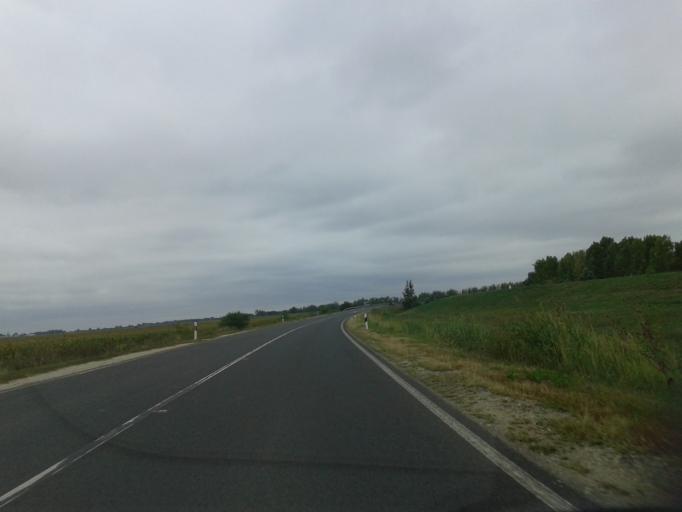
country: HU
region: Bacs-Kiskun
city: Solt
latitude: 46.7590
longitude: 19.0108
